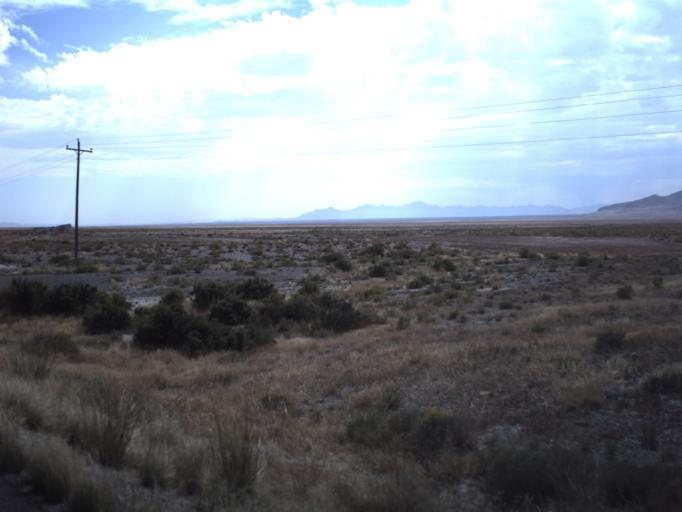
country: US
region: Utah
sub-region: Tooele County
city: Wendover
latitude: 41.4271
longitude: -113.8361
